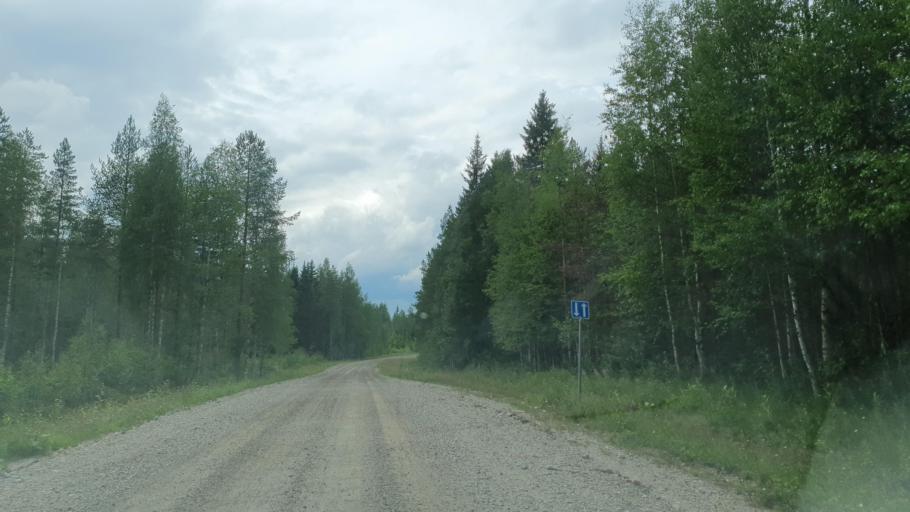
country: FI
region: Kainuu
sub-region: Kehys-Kainuu
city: Kuhmo
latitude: 64.4879
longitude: 29.7085
